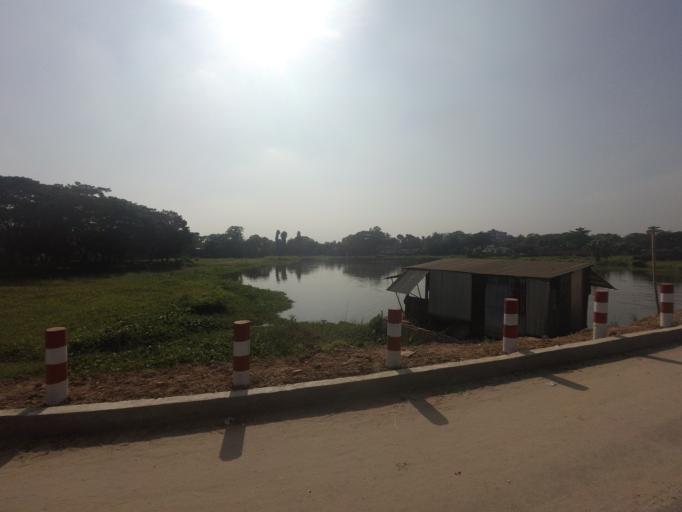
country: BD
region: Dhaka
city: Azimpur
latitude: 23.7340
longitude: 90.3324
